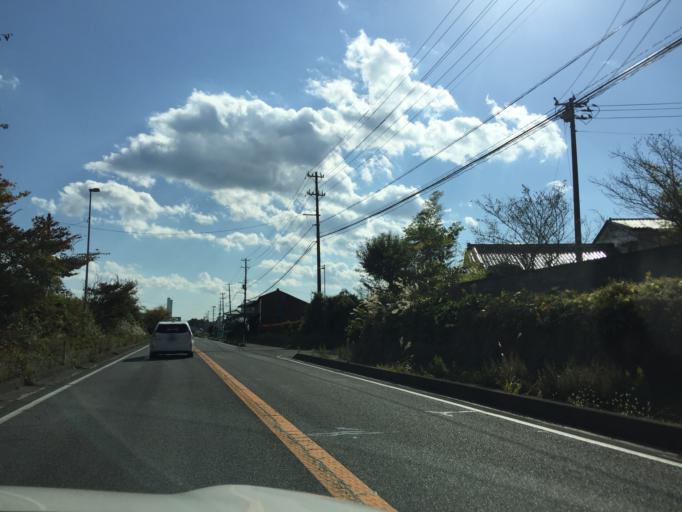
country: JP
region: Fukushima
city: Namie
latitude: 37.2654
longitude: 140.9960
